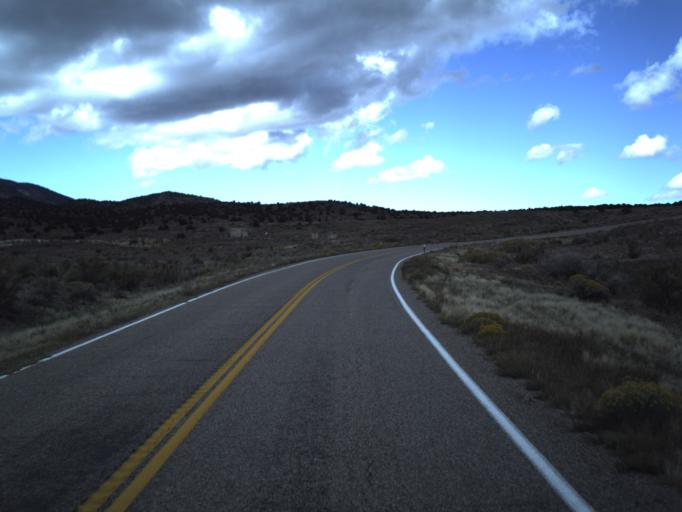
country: US
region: Utah
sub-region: Beaver County
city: Milford
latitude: 38.4546
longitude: -113.2592
